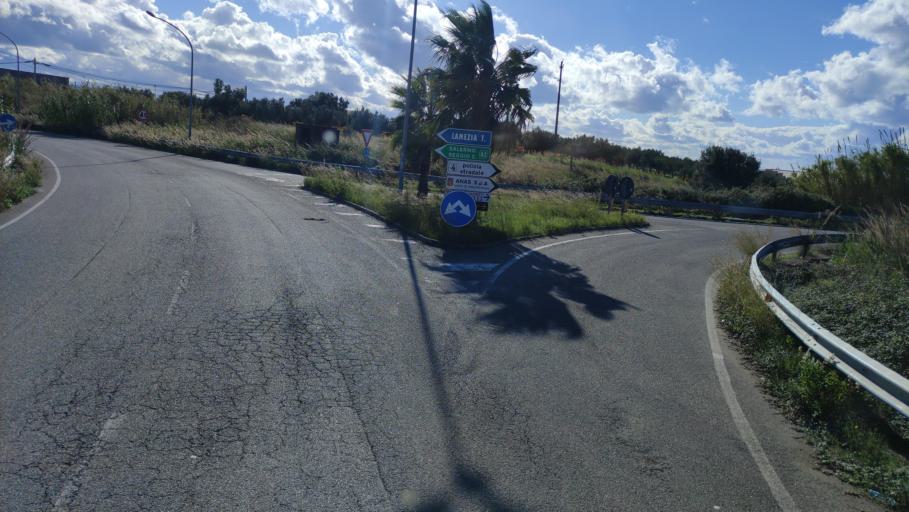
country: IT
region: Calabria
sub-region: Provincia di Catanzaro
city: Santa Eufemia Lamezia
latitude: 38.9202
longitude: 16.2723
